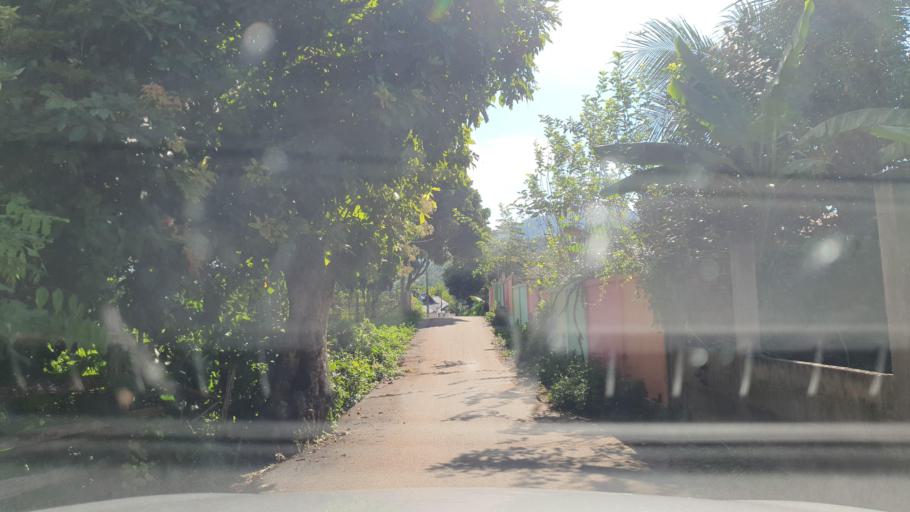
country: TH
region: Chiang Mai
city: Mae On
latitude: 18.7371
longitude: 99.3058
